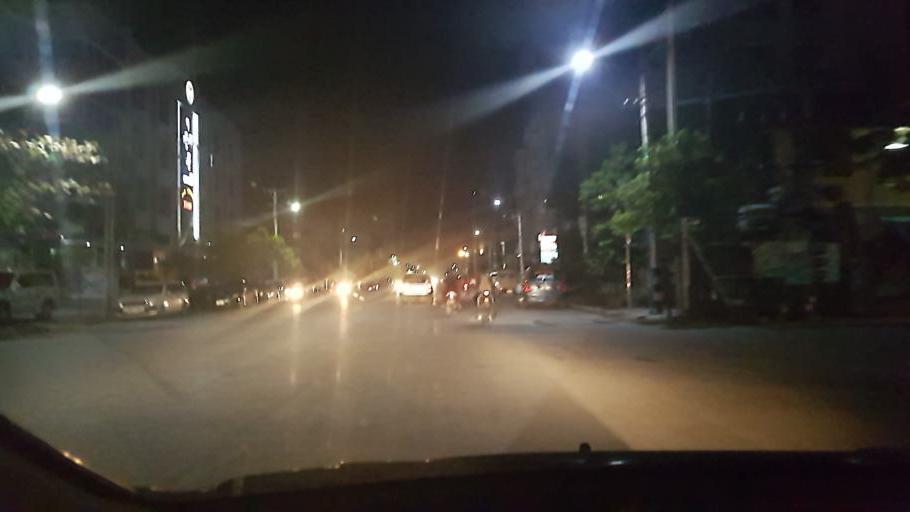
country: MM
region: Mandalay
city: Mandalay
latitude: 21.9777
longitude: 96.0957
